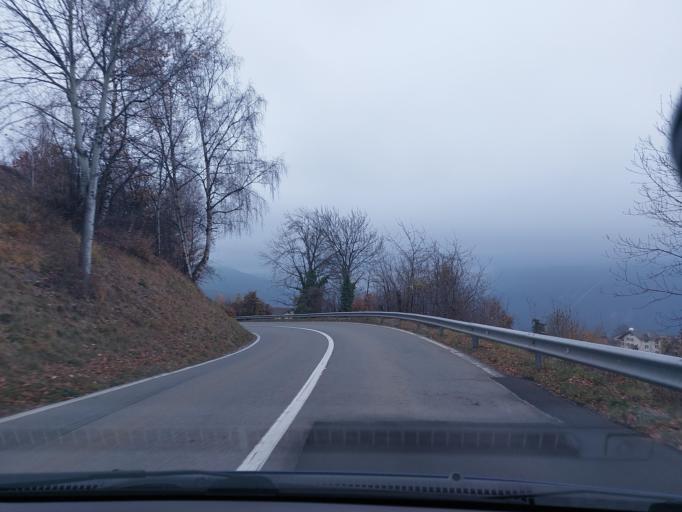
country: CH
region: Valais
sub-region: Sierre District
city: Veyras
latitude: 46.3143
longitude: 7.5240
